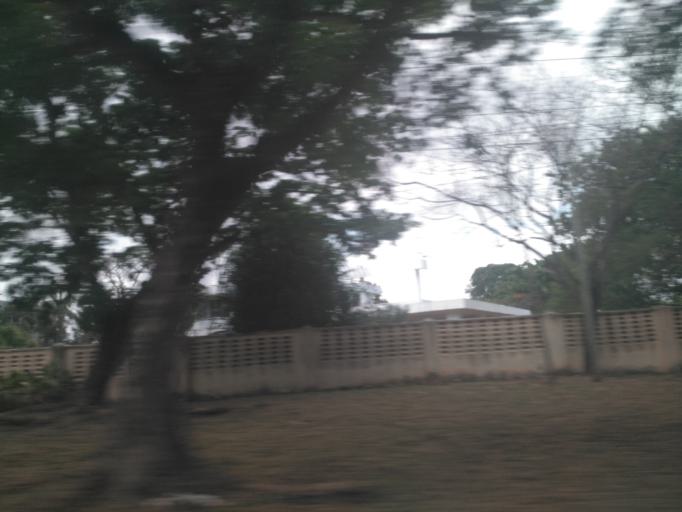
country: TZ
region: Dar es Salaam
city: Magomeni
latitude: -6.7633
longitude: 39.2795
